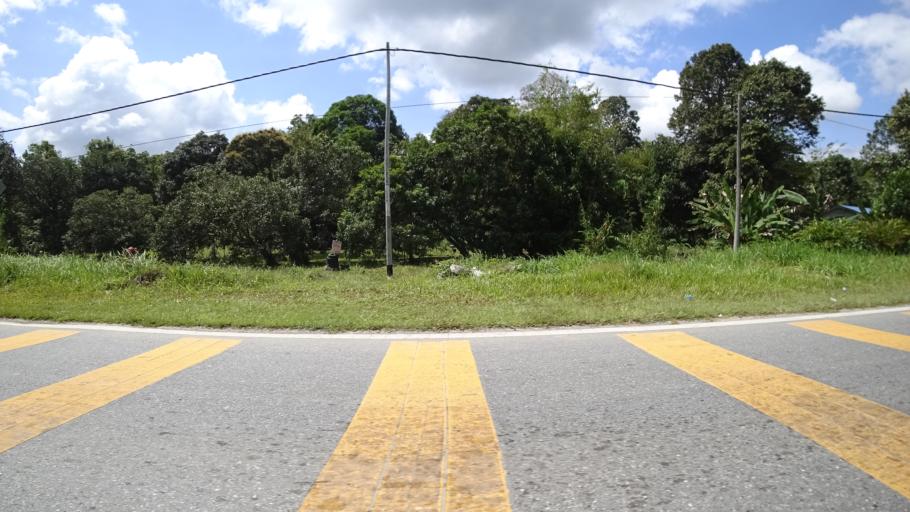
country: MY
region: Sarawak
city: Limbang
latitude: 4.6580
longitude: 114.9551
